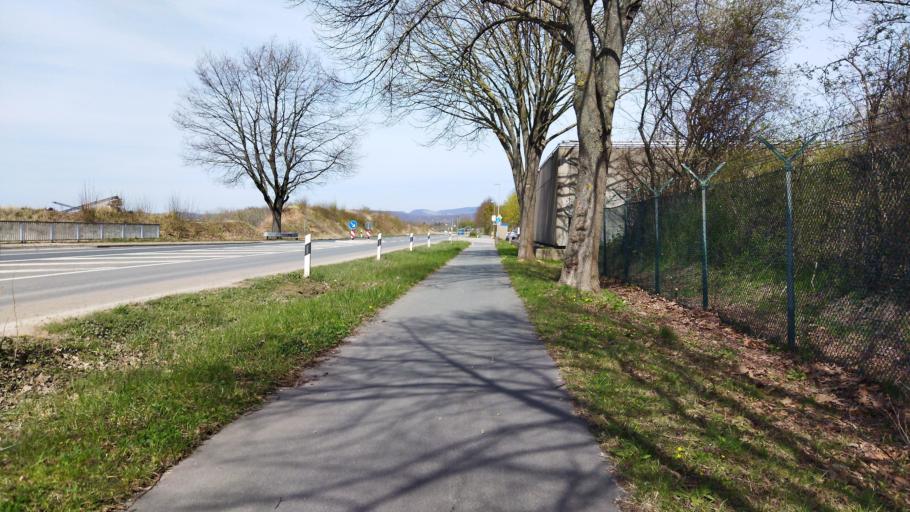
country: DE
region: Lower Saxony
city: Hameln
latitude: 52.0790
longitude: 9.3784
